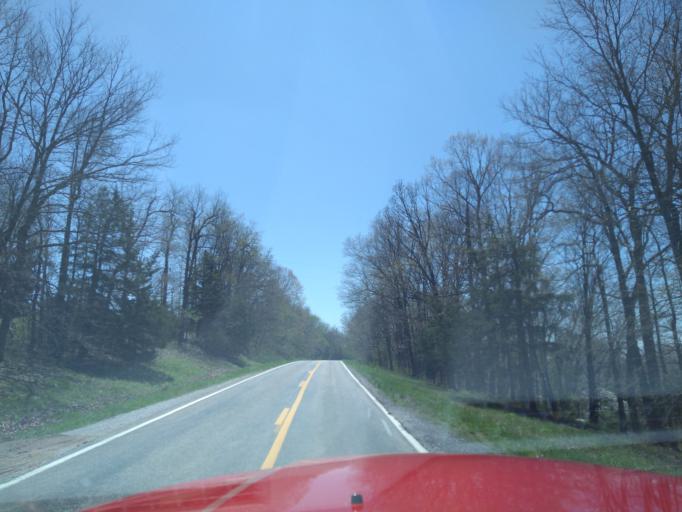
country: US
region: Arkansas
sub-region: Washington County
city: West Fork
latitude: 35.8140
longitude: -94.2578
